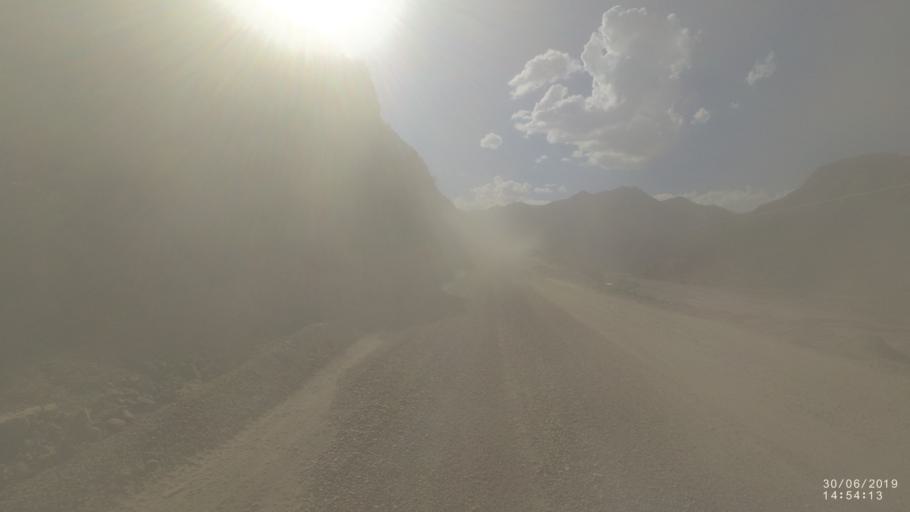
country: BO
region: Cochabamba
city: Irpa Irpa
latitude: -17.7599
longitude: -66.3496
